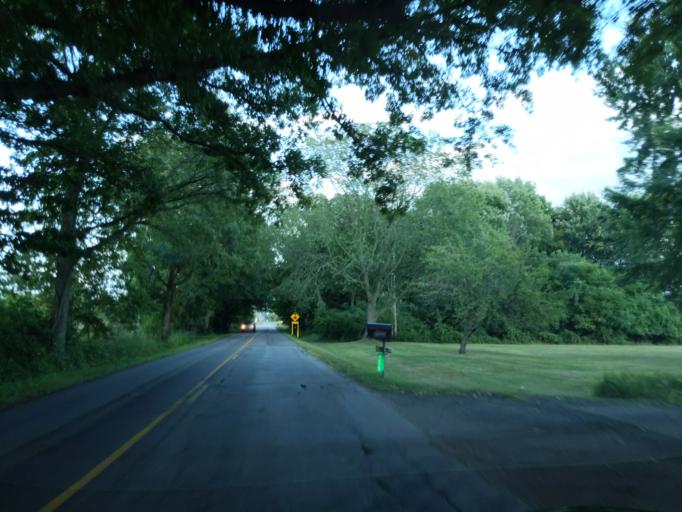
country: US
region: Michigan
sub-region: Ingham County
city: Holt
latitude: 42.6111
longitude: -84.5060
